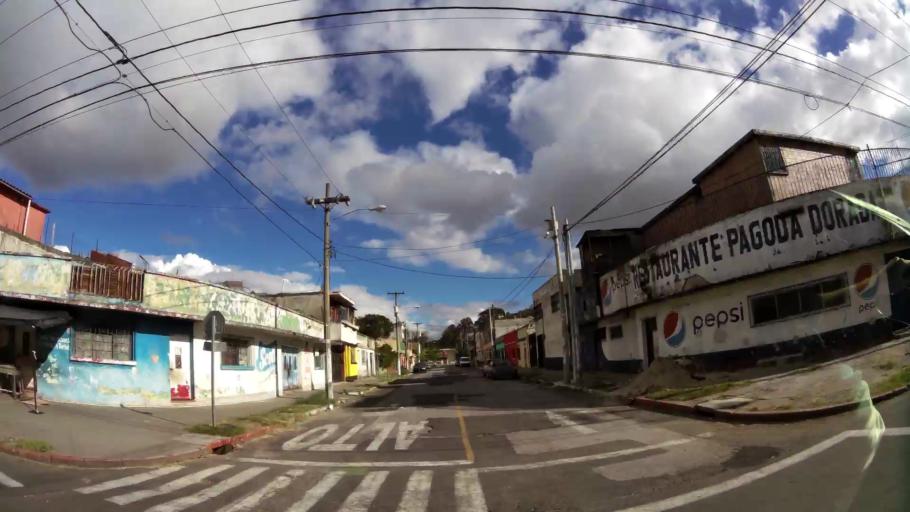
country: GT
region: Guatemala
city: Guatemala City
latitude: 14.6153
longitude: -90.5464
